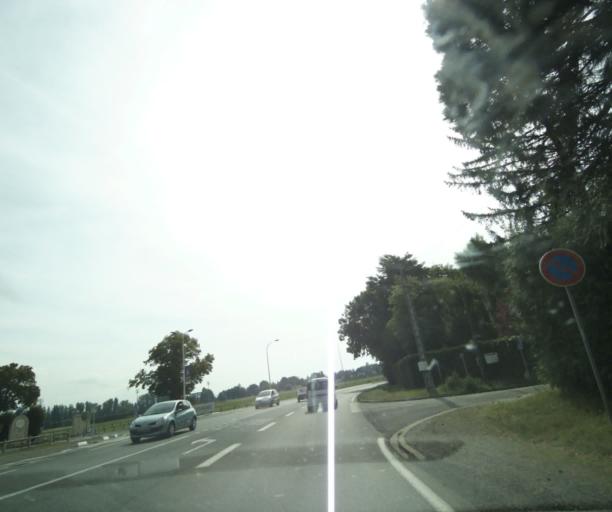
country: FR
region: Auvergne
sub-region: Departement de l'Allier
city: Bellerive-sur-Allier
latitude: 46.1309
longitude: 3.4017
